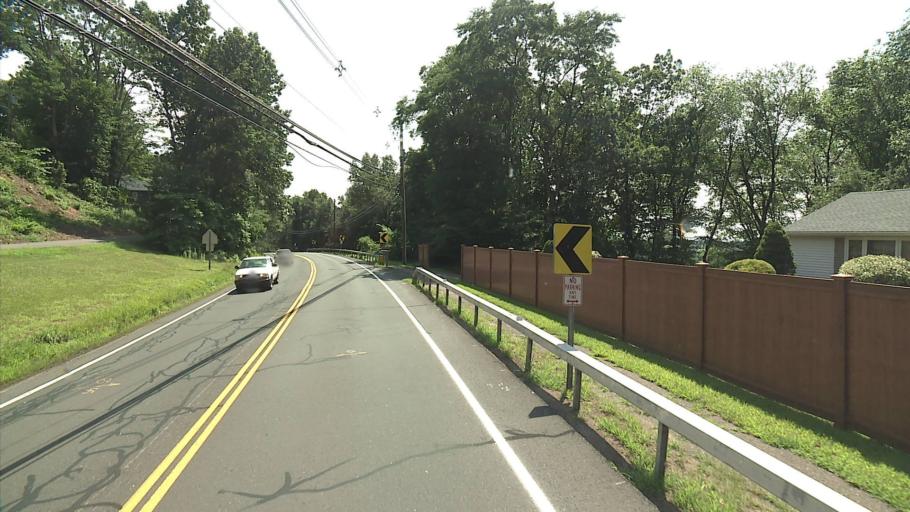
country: US
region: Connecticut
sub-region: Tolland County
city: Rockville
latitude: 41.8504
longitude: -72.4672
